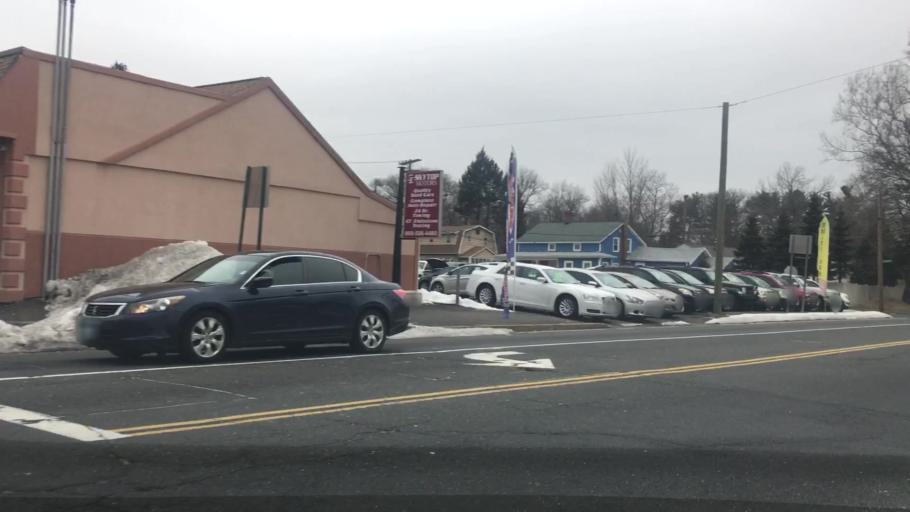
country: US
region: Connecticut
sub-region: Hartford County
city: Bristol
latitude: 41.6723
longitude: -72.9129
